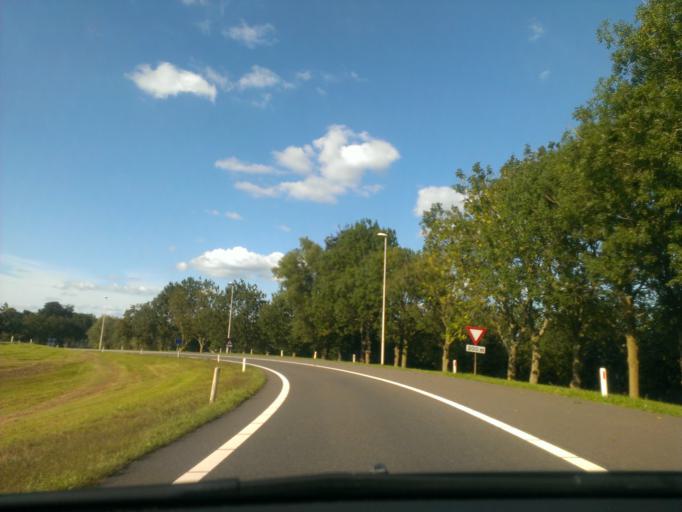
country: NL
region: Gelderland
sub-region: Gemeente Heerde
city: Heerde
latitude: 52.3719
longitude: 6.0256
